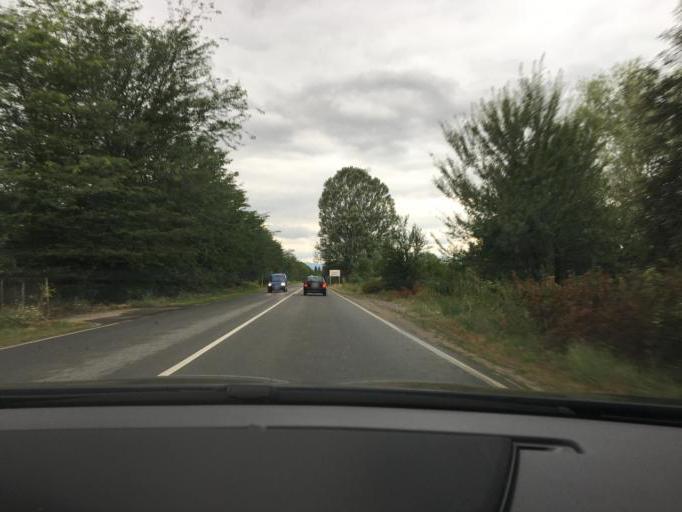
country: BG
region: Kyustendil
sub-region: Obshtina Kyustendil
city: Kyustendil
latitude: 42.2577
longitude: 22.8403
